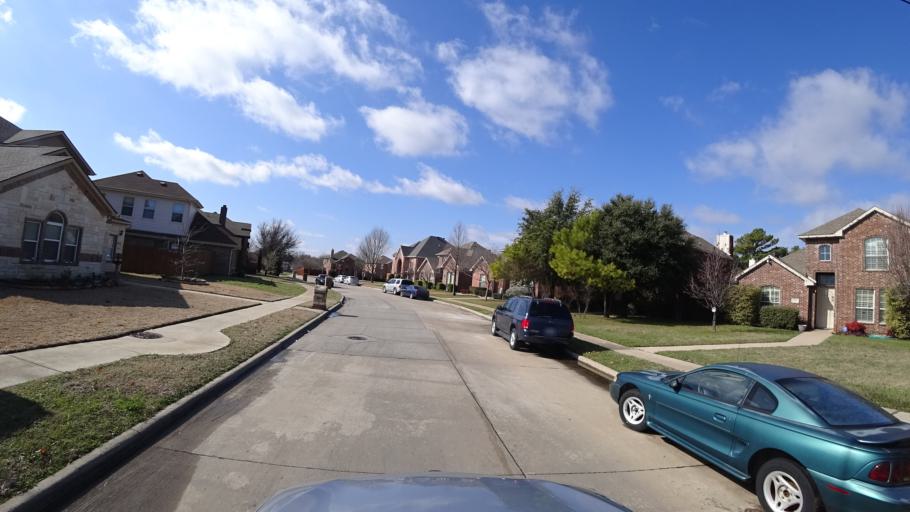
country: US
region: Texas
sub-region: Denton County
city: Lewisville
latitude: 33.0333
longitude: -97.0016
